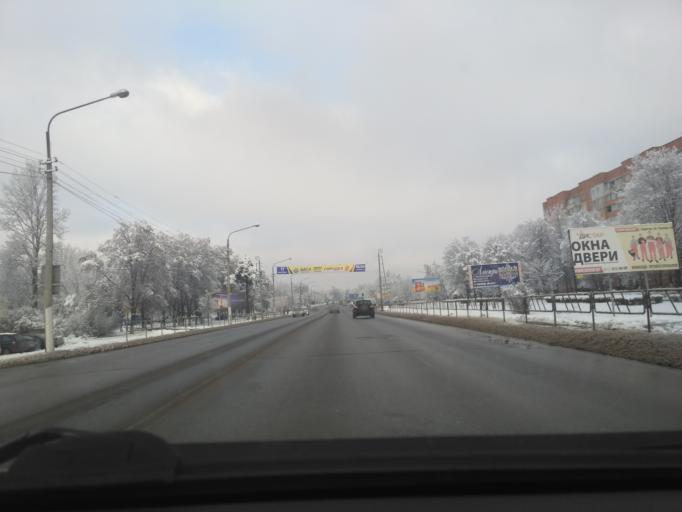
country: BY
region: Minsk
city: Horad Barysaw
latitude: 54.2214
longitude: 28.4925
